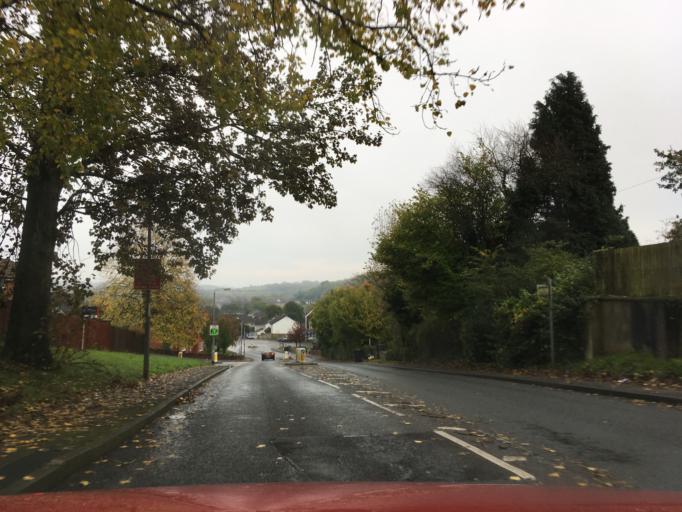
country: GB
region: Wales
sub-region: Newport
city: Caerleon
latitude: 51.5979
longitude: -2.9394
